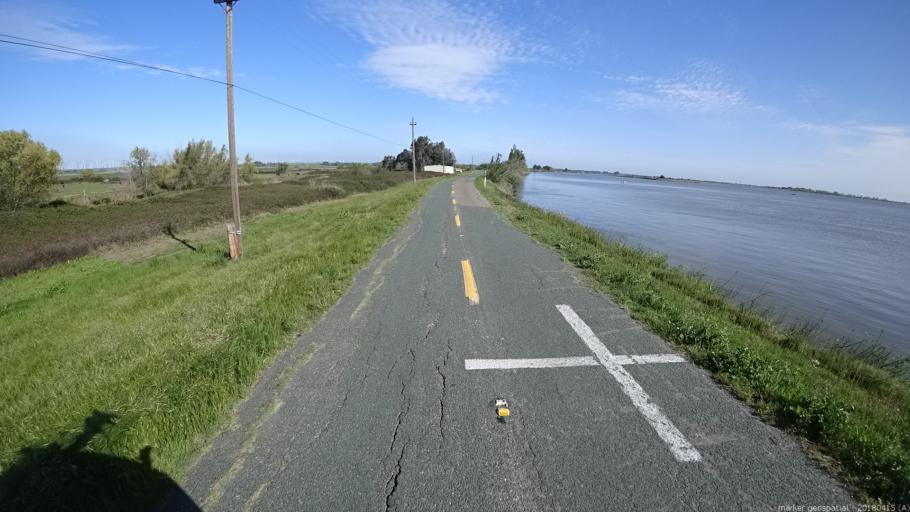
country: US
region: California
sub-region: Solano County
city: Rio Vista
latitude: 38.0807
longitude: -121.6850
